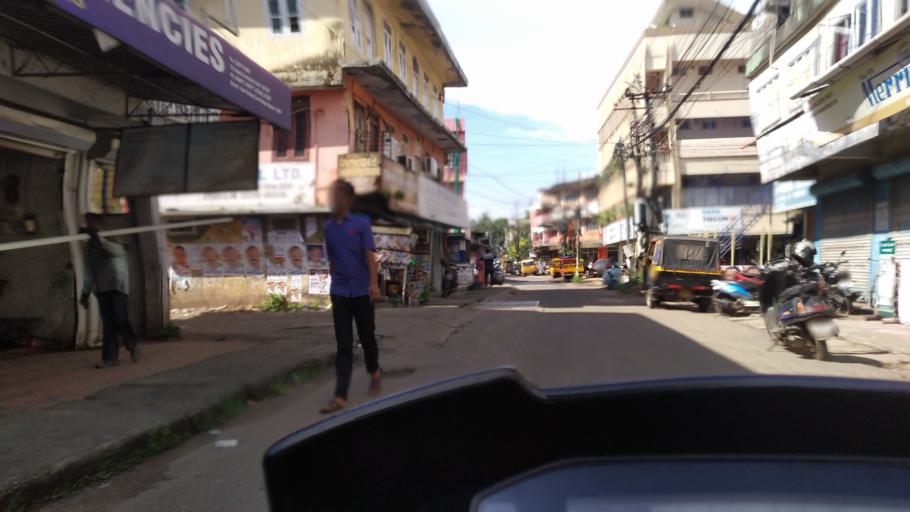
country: IN
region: Kerala
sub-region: Ernakulam
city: Cochin
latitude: 9.9782
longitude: 76.2816
